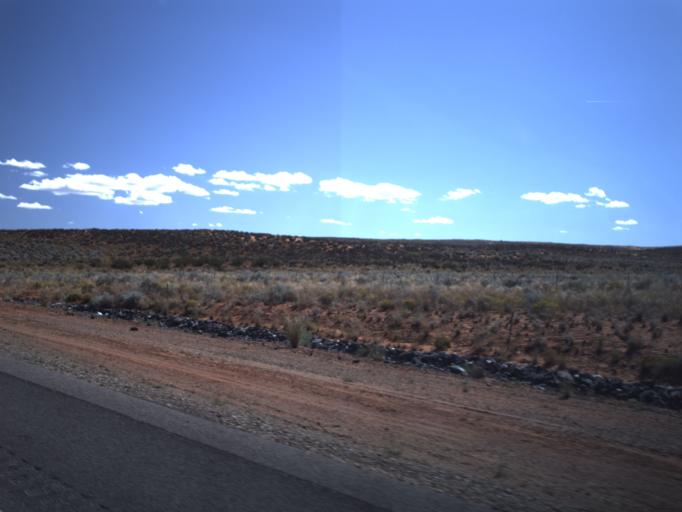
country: US
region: Utah
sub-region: Washington County
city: Washington
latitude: 37.1103
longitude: -113.4200
